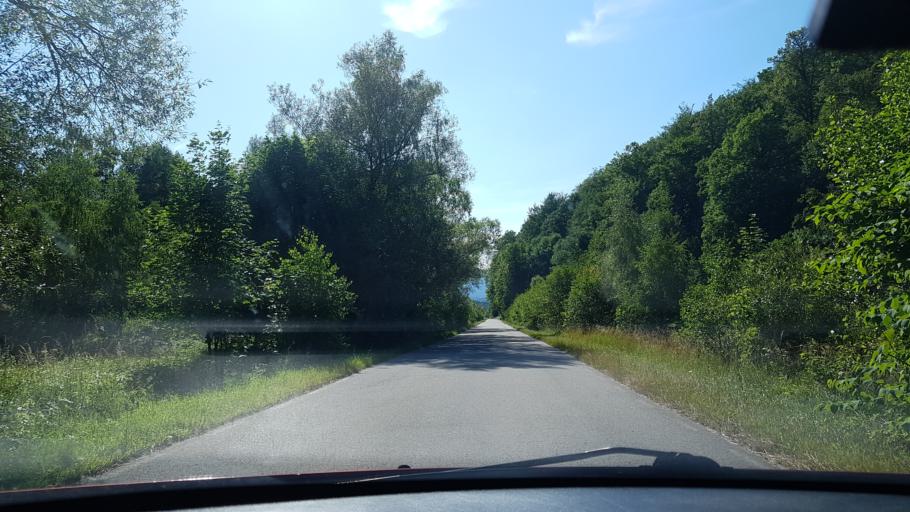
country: PL
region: Lower Silesian Voivodeship
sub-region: Powiat klodzki
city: Miedzylesie
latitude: 50.2330
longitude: 16.7336
